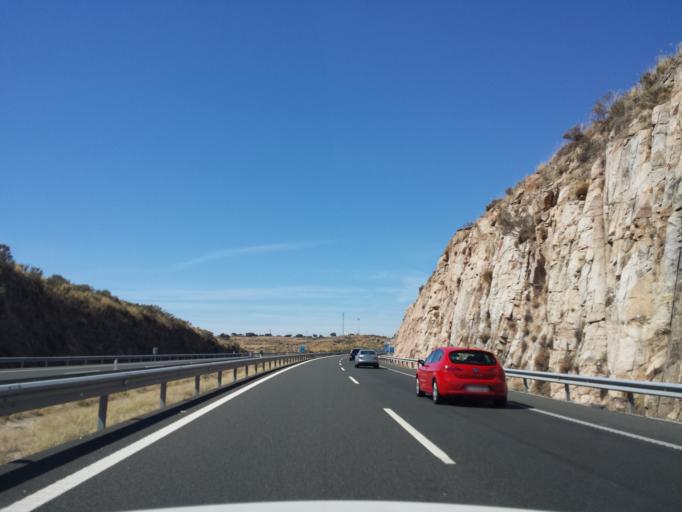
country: ES
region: Extremadura
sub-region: Provincia de Caceres
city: Navalmoral de la Mata
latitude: 39.8788
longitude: -5.5403
